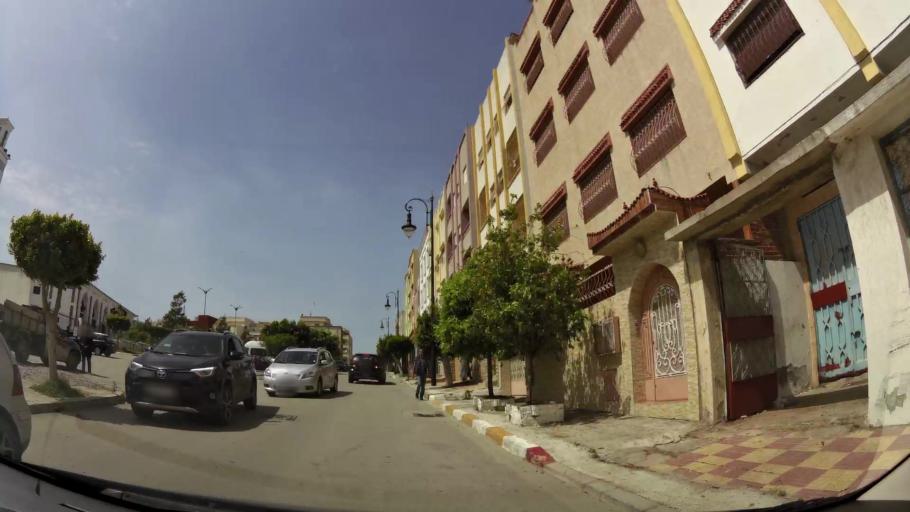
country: MA
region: Tanger-Tetouan
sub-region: Tanger-Assilah
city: Tangier
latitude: 35.7575
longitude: -5.8346
